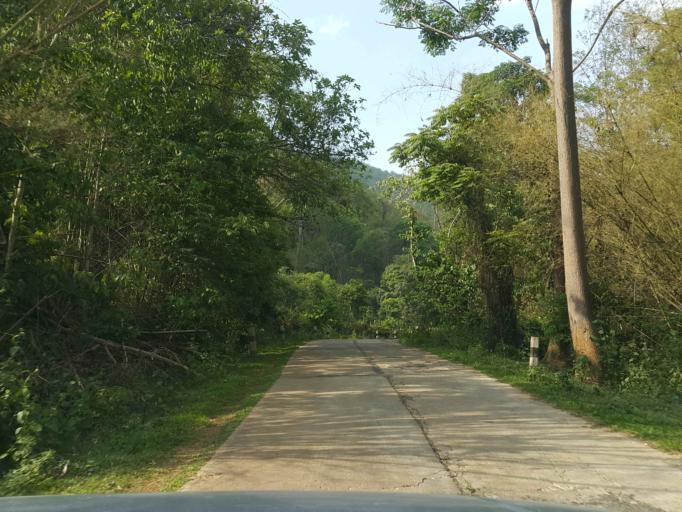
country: TH
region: Chiang Mai
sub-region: Amphoe Chiang Dao
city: Chiang Dao
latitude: 19.4067
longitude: 98.7865
